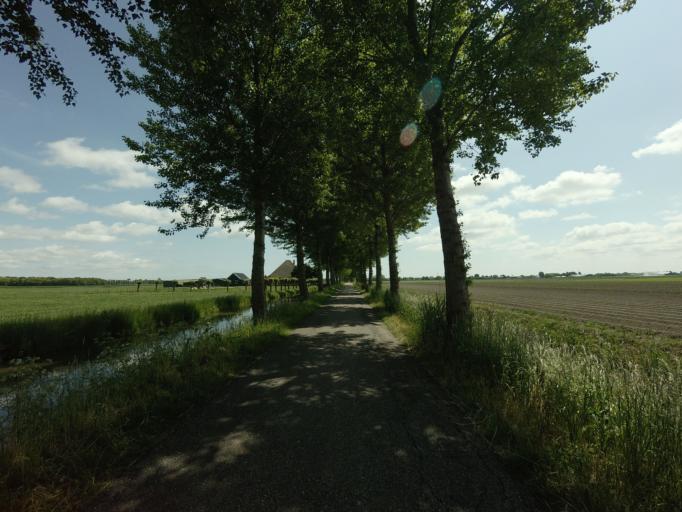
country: NL
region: North Holland
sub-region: Gemeente Beemster
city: Halfweg
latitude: 52.5990
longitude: 4.9265
